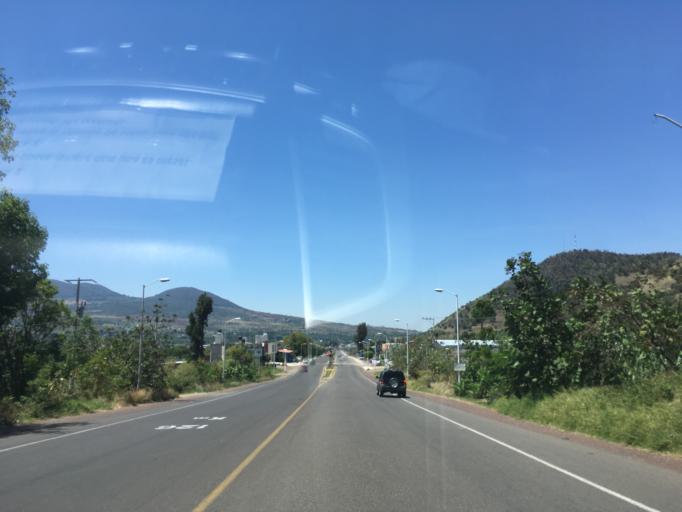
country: MX
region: Michoacan
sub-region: Tuxpan
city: Santa Ana
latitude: 19.5850
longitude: -100.4664
